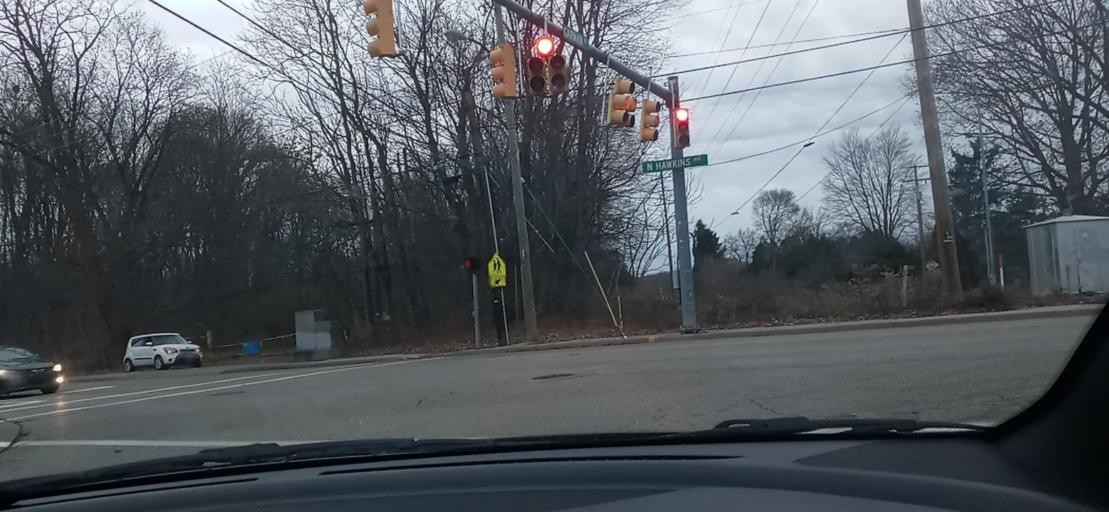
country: US
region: Ohio
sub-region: Summit County
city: Fairlawn
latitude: 41.1154
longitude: -81.5690
